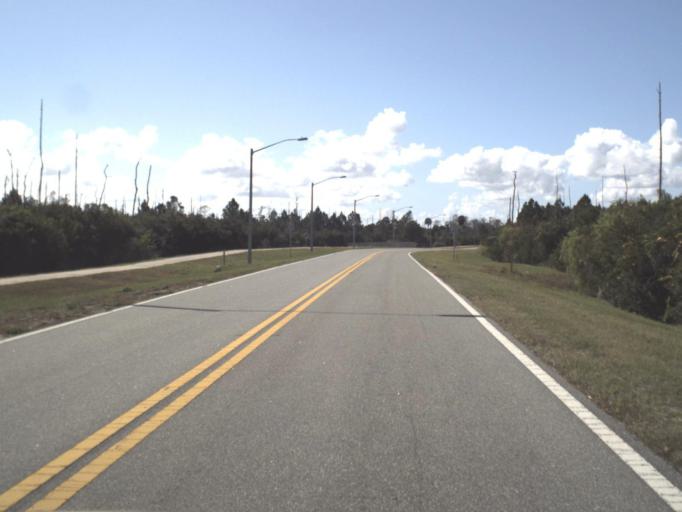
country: US
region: Florida
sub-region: Flagler County
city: Palm Coast
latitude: 29.6023
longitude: -81.2405
